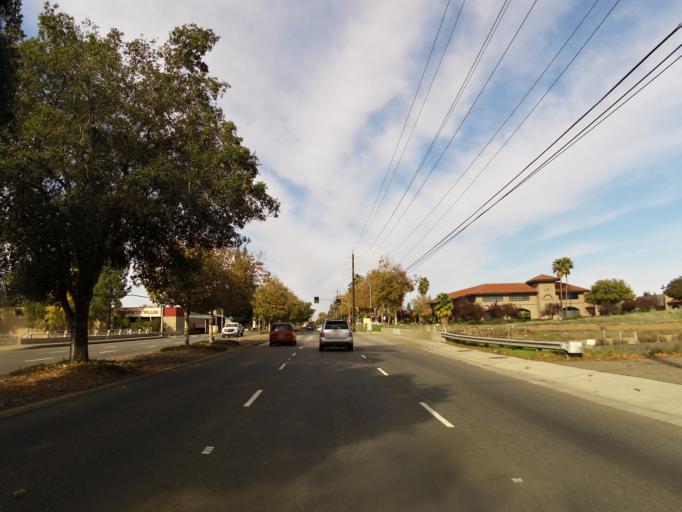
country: US
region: California
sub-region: Sacramento County
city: Gold River
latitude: 38.5951
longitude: -121.2655
